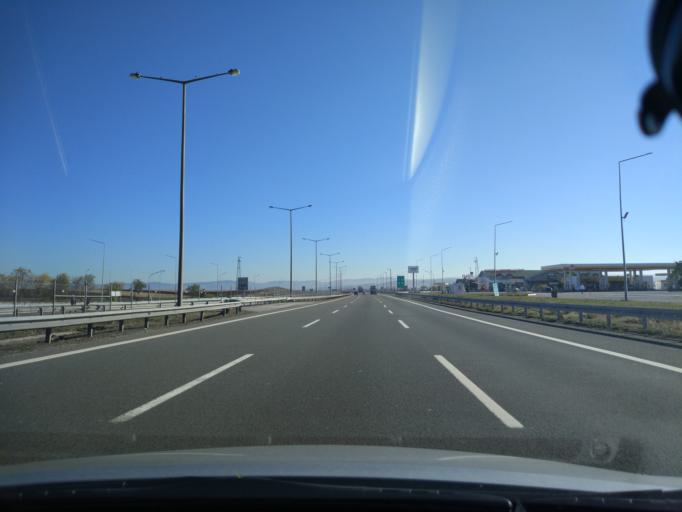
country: TR
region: Bolu
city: Dortdivan
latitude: 40.7502
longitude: 32.0822
